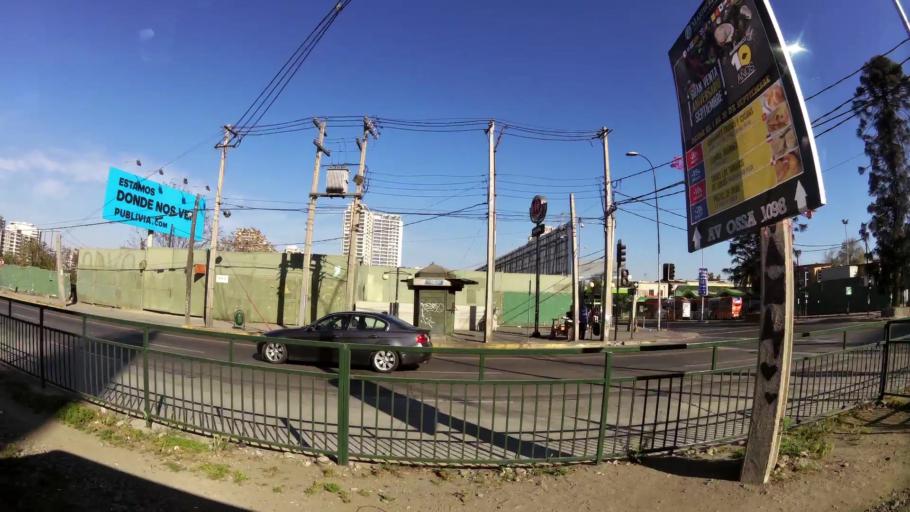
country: CL
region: Santiago Metropolitan
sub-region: Provincia de Santiago
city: Villa Presidente Frei, Nunoa, Santiago, Chile
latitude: -33.4538
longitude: -70.5709
